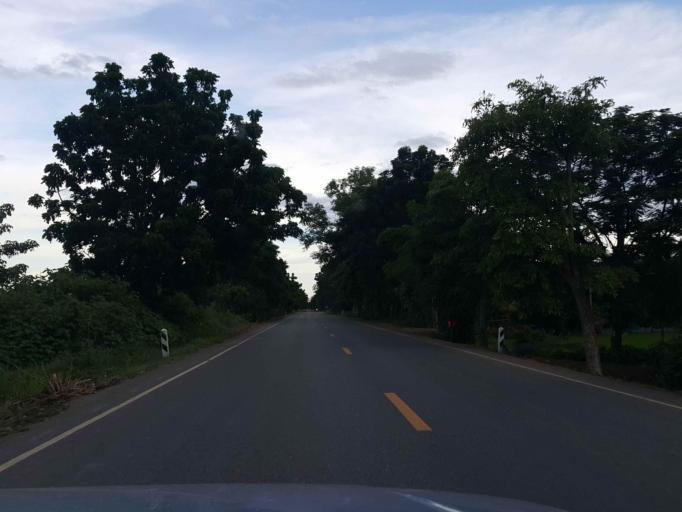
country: TH
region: Sukhothai
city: Sawankhalok
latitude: 17.3501
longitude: 99.7425
